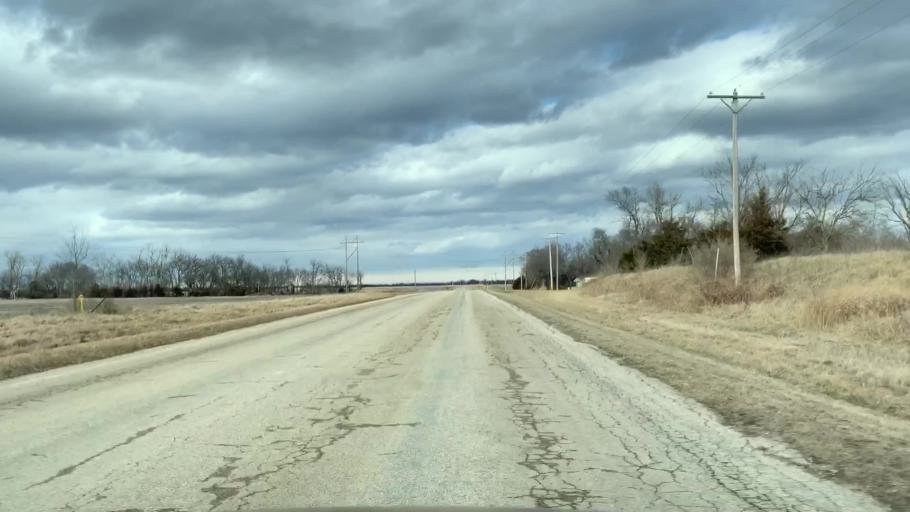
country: US
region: Kansas
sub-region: Allen County
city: Humboldt
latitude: 37.7667
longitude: -95.4706
